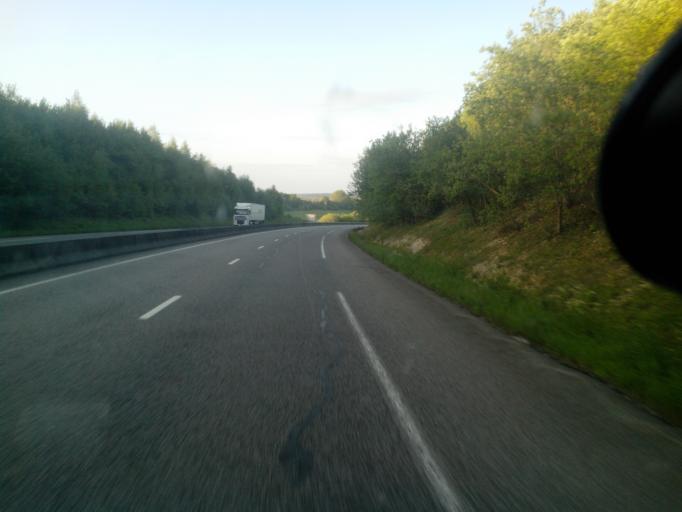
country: FR
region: Haute-Normandie
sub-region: Departement de la Seine-Maritime
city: Foucarmont
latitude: 49.8368
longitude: 1.5305
